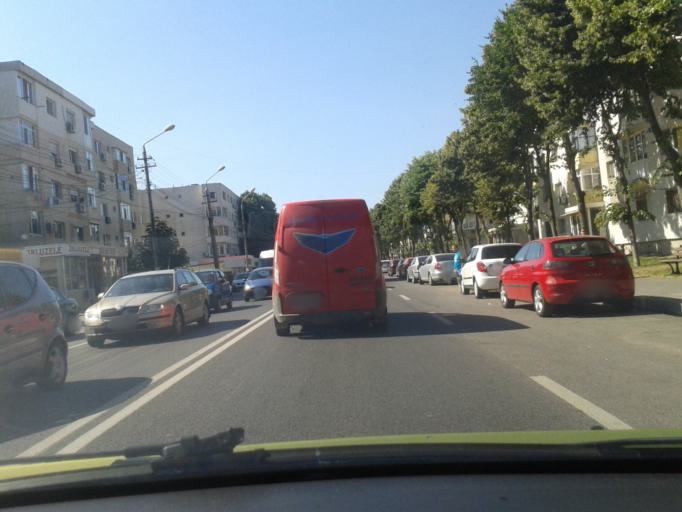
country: RO
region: Constanta
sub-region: Municipiul Mangalia
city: Mangalia
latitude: 43.8213
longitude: 28.5827
